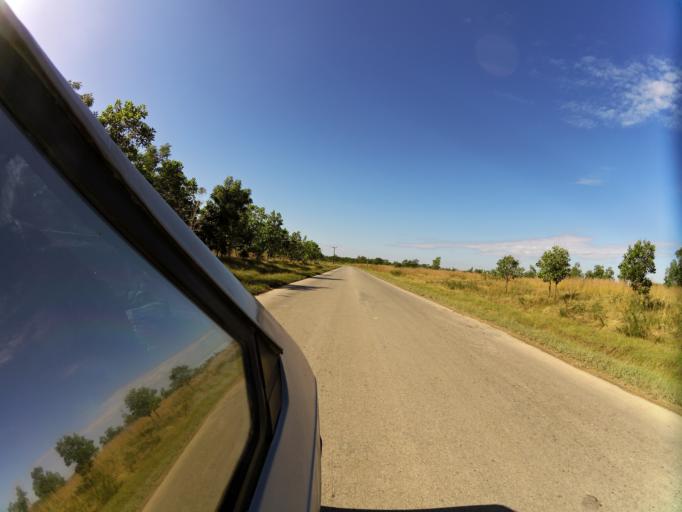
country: CU
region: Las Tunas
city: Las Tunas
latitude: 20.9804
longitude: -76.9007
